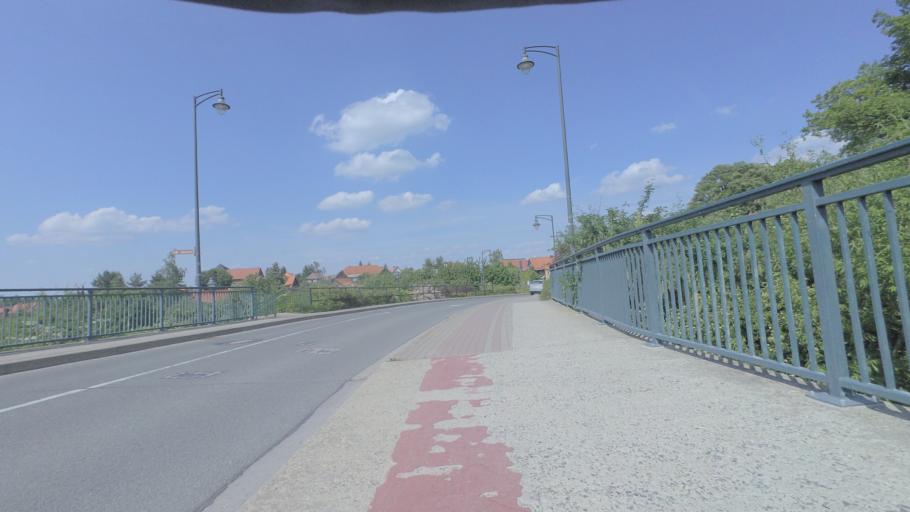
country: DE
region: Saxony-Anhalt
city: Darlingerode
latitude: 51.8488
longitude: 10.7343
